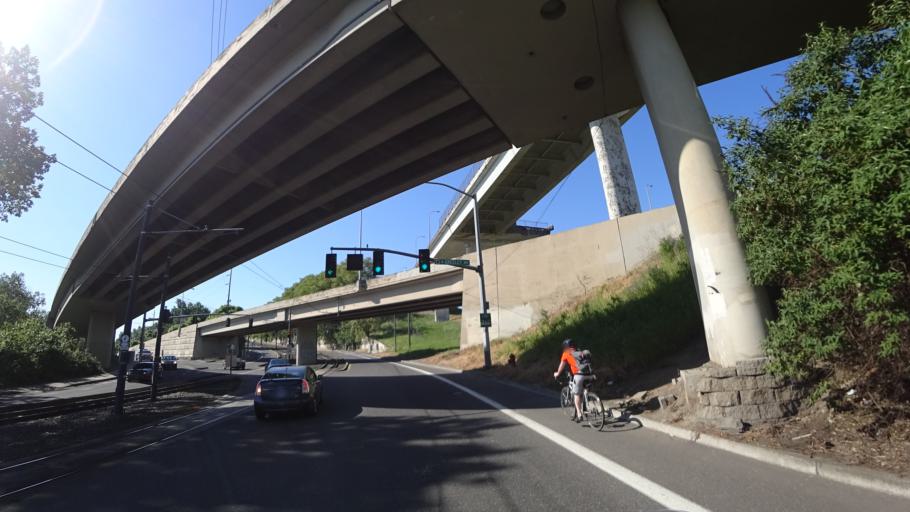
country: US
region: Oregon
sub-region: Multnomah County
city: Portland
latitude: 45.5445
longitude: -122.6773
